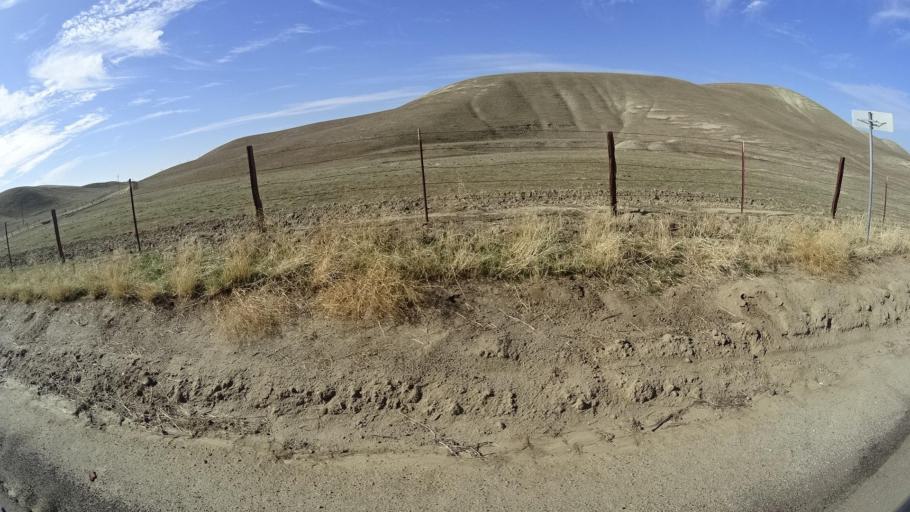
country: US
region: California
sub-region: Tulare County
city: Richgrove
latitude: 35.6387
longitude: -118.9432
